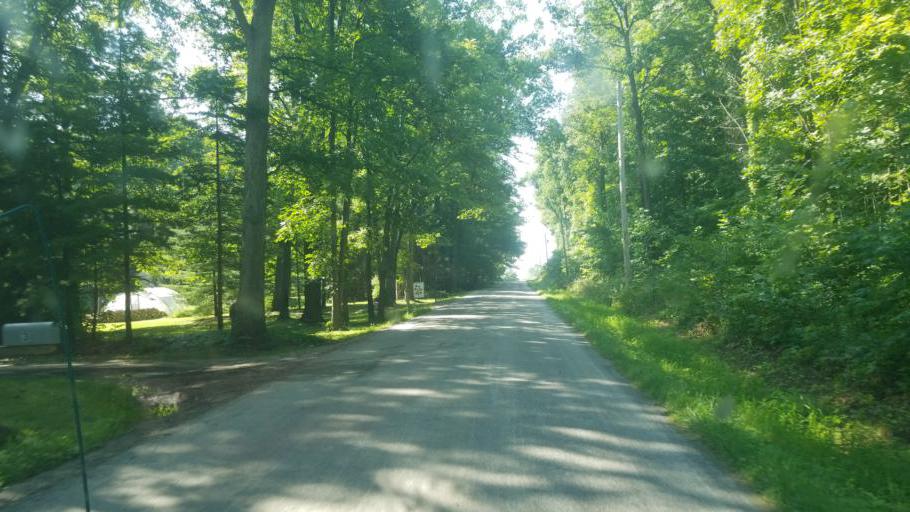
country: US
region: Ohio
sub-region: Lorain County
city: Wellington
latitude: 41.0637
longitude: -82.2016
